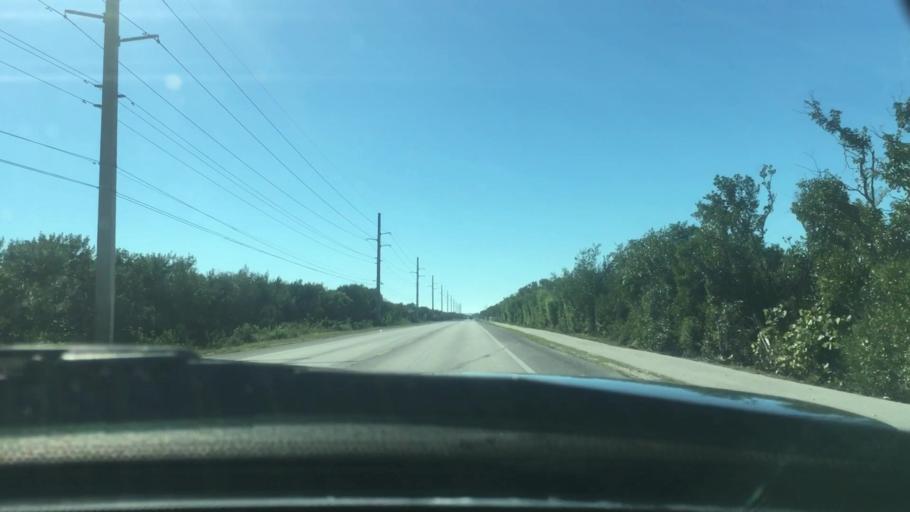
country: US
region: Florida
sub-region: Monroe County
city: Big Pine Key
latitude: 24.6681
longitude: -81.2554
